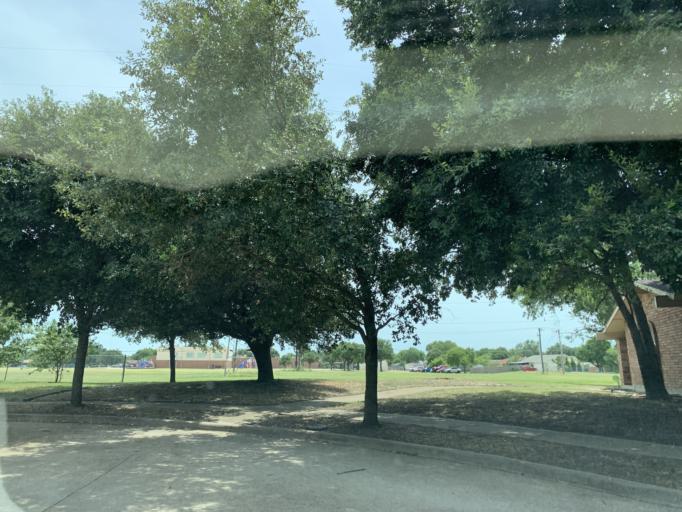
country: US
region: Texas
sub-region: Dallas County
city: Grand Prairie
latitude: 32.6569
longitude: -97.0314
